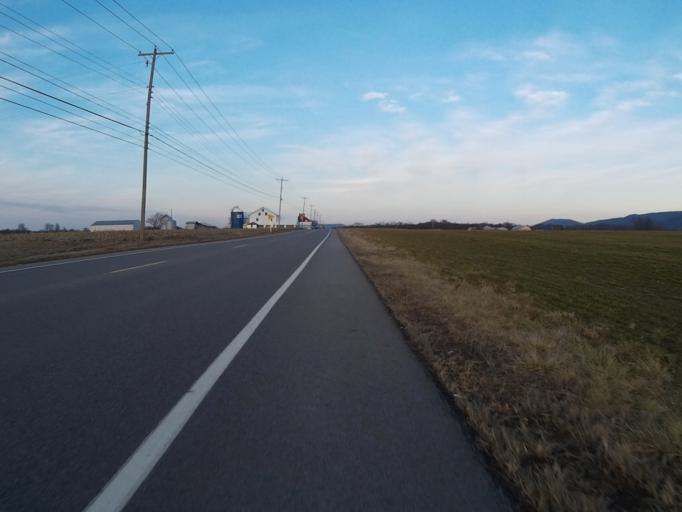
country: US
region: Pennsylvania
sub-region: Centre County
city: Pine Grove Mills
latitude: 40.7467
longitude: -77.9012
